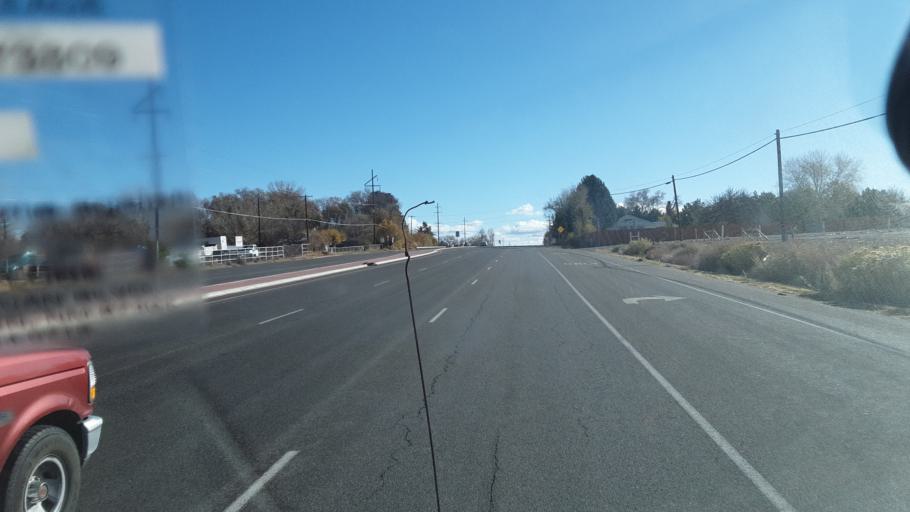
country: US
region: New Mexico
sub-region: San Juan County
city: Lee Acres
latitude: 36.7010
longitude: -108.0588
